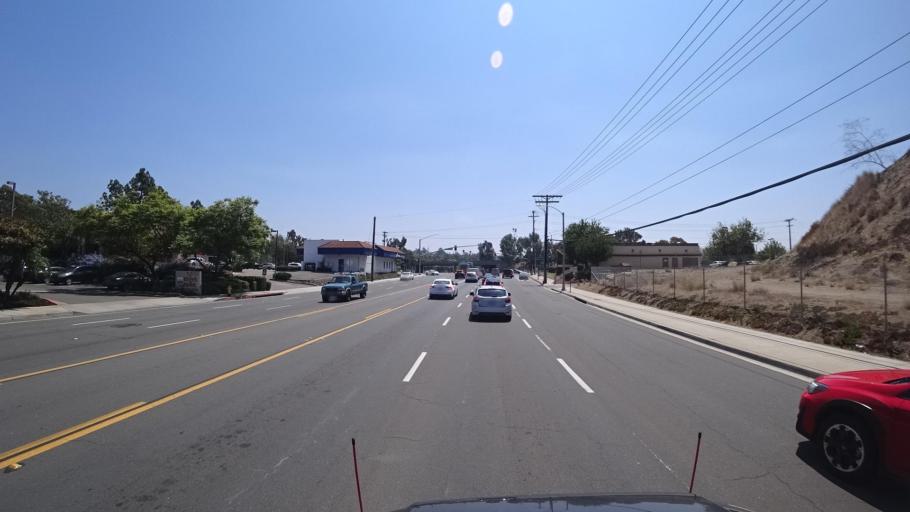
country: US
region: California
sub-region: San Diego County
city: Vista
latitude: 33.1964
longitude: -117.2551
